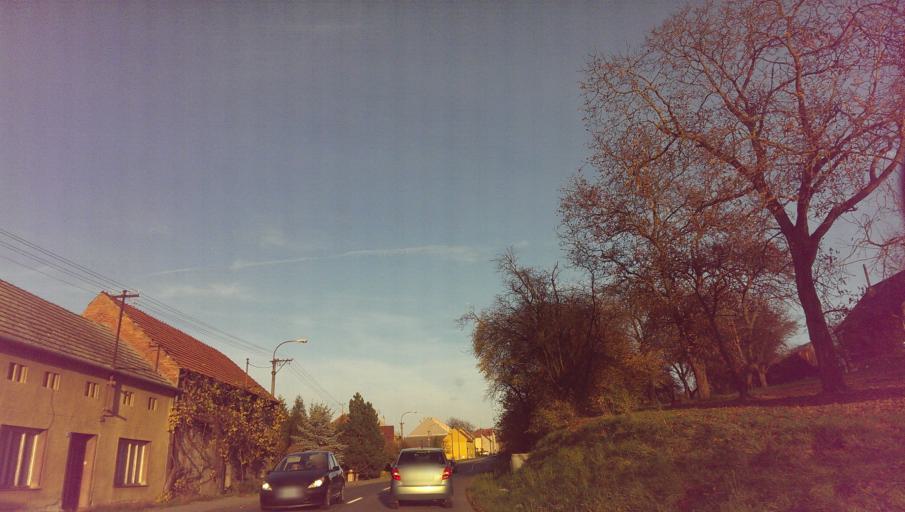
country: CZ
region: Zlin
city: Mistrice
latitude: 49.0973
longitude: 17.5378
